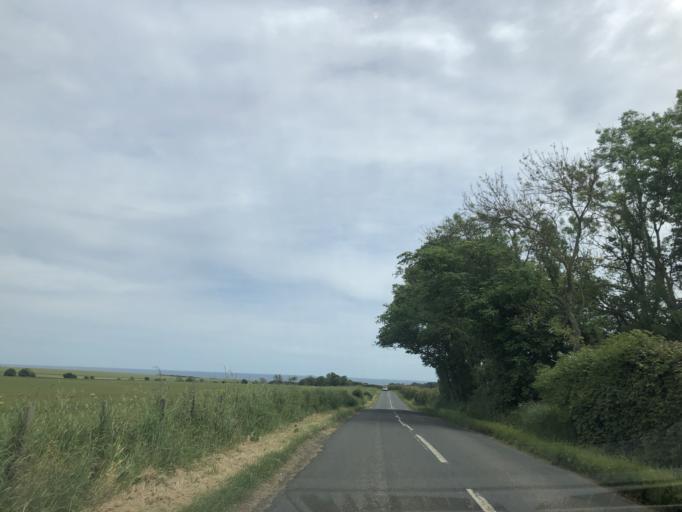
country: GB
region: Scotland
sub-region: Fife
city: Anstruther
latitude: 56.2660
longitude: -2.6489
